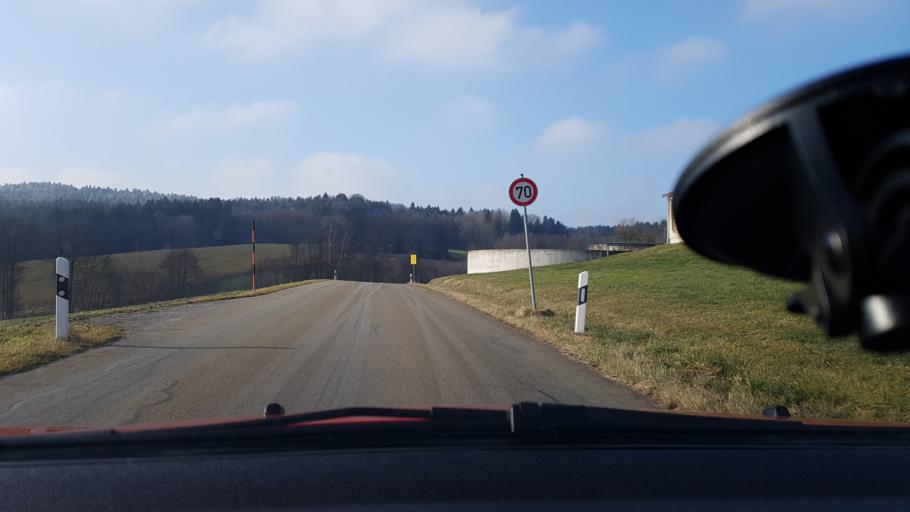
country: DE
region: Bavaria
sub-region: Lower Bavaria
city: Stubenberg
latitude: 48.3105
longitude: 13.0437
